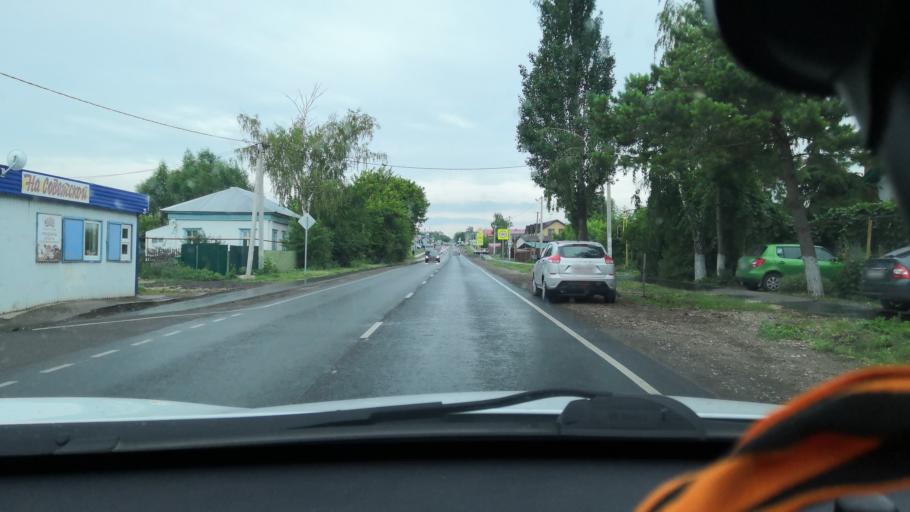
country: RU
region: Samara
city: Novosemeykino
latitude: 53.3784
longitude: 50.3439
